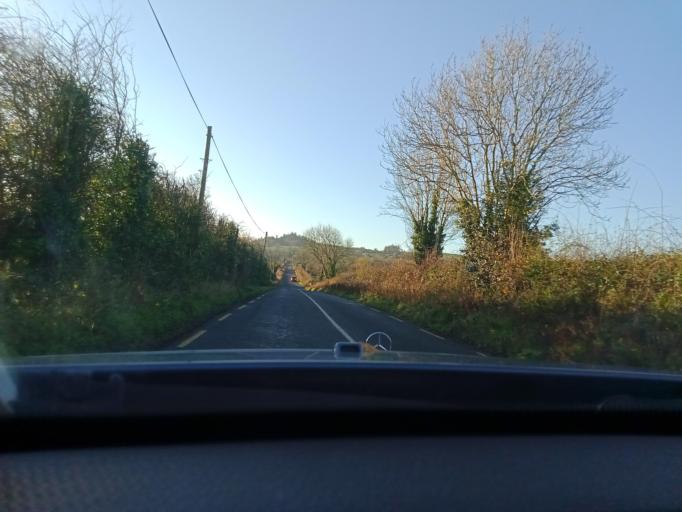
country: IE
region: Leinster
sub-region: Kilkenny
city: Callan
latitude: 52.4730
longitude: -7.3932
